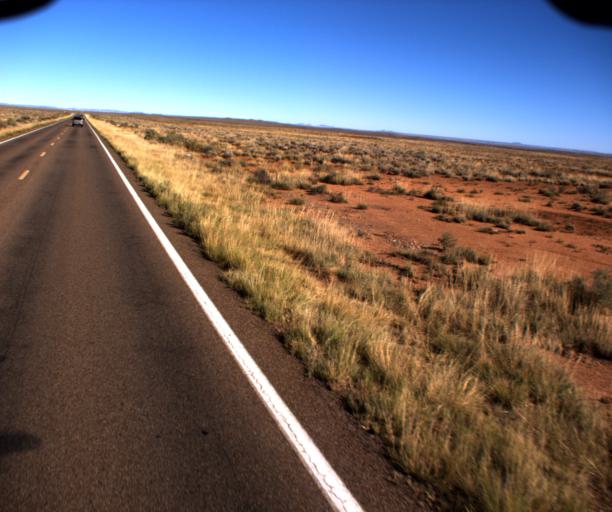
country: US
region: Arizona
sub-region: Navajo County
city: Holbrook
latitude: 34.7544
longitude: -110.1231
